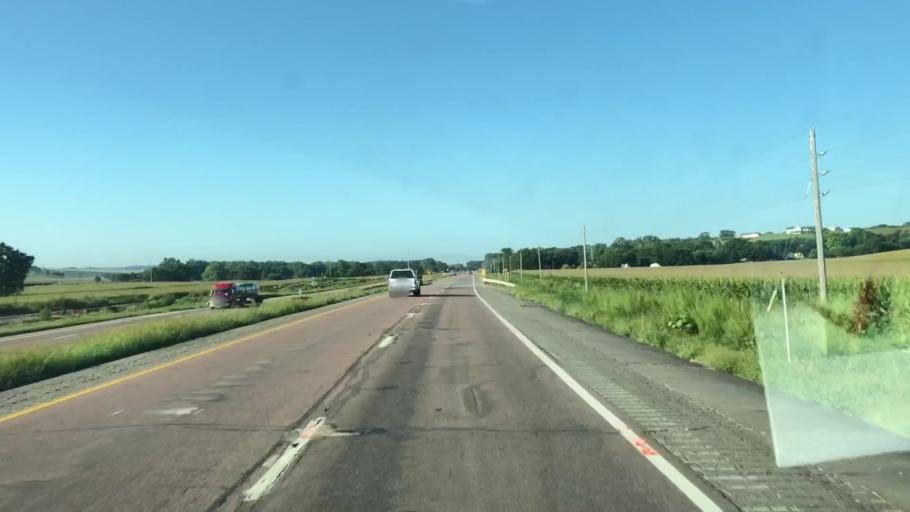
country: US
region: Iowa
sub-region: Woodbury County
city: Sioux City
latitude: 42.5818
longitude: -96.3120
